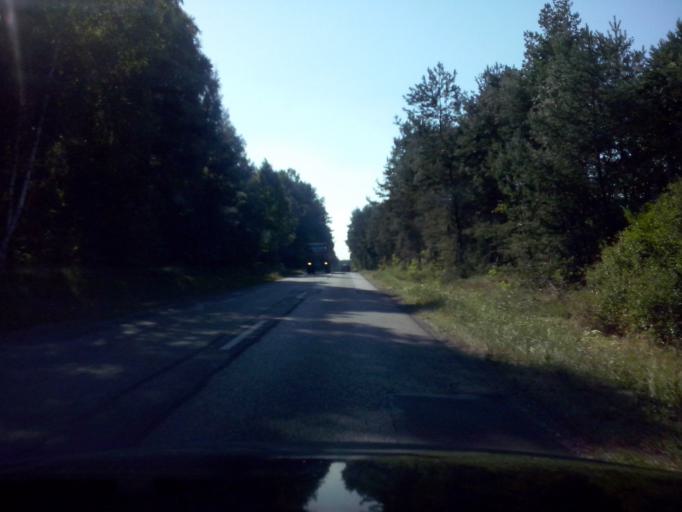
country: PL
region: Swietokrzyskie
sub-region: Powiat kielecki
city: Daleszyce
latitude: 50.8119
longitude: 20.7413
